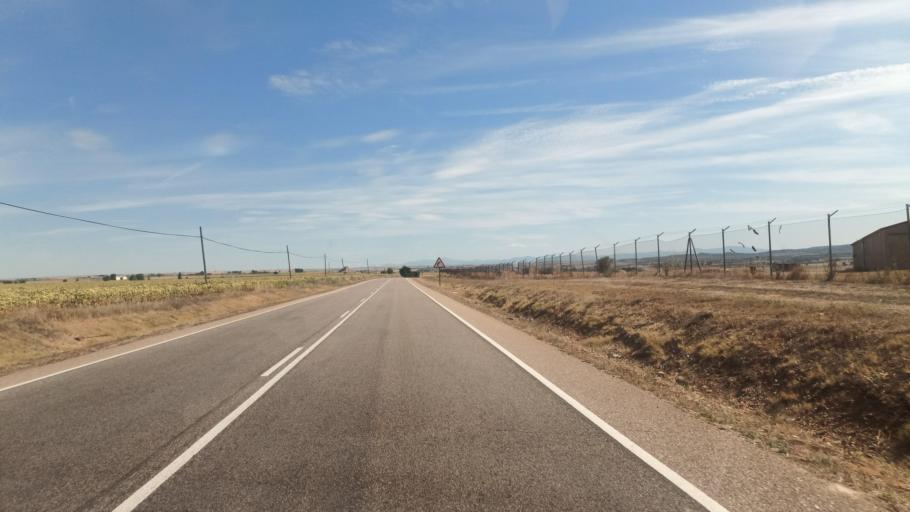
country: ES
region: Castille and Leon
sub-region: Provincia de Burgos
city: Quintanabureba
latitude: 42.6316
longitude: -3.3779
